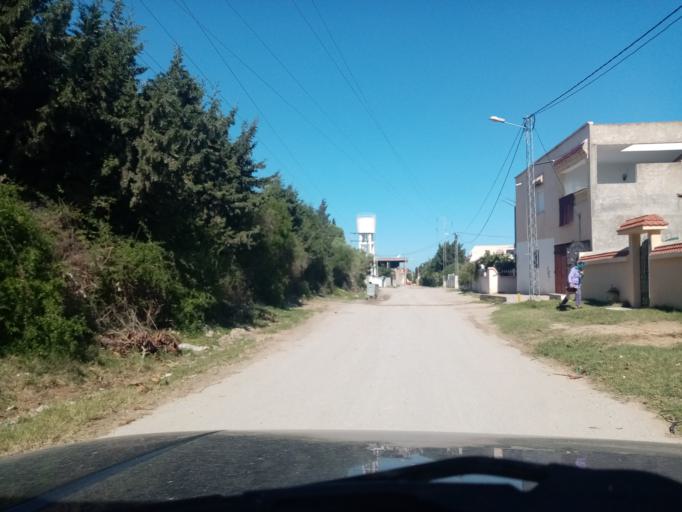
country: TN
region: Nabul
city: Bu `Urqub
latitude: 36.5737
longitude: 10.5736
